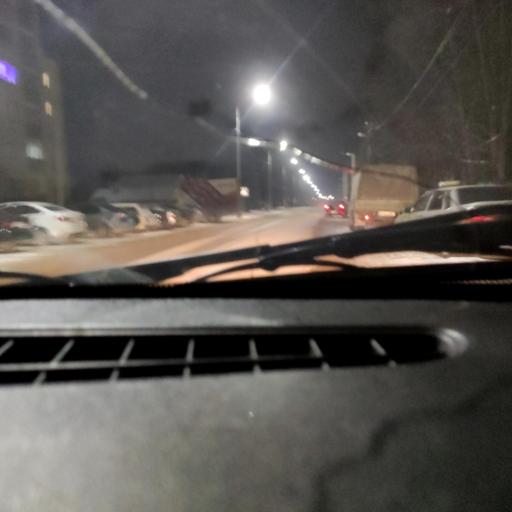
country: RU
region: Bashkortostan
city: Avdon
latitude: 54.6094
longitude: 55.8424
